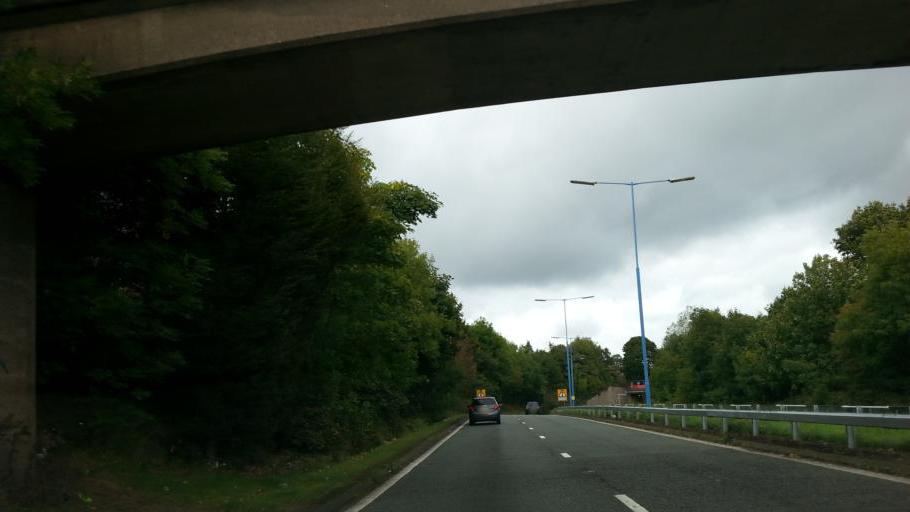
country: GB
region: England
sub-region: City and Borough of Birmingham
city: Bartley Green
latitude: 52.4597
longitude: -2.0088
